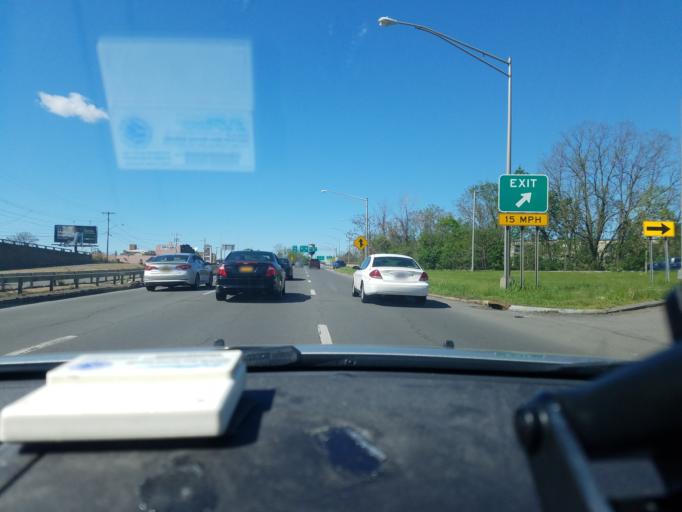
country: US
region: New York
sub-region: Onondaga County
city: Syracuse
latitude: 43.0508
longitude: -76.1588
